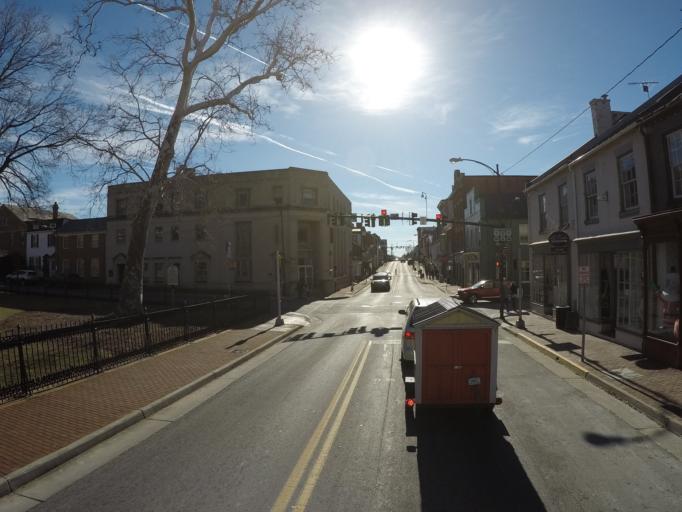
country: US
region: Virginia
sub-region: Loudoun County
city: Leesburg
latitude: 39.1157
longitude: -77.5644
